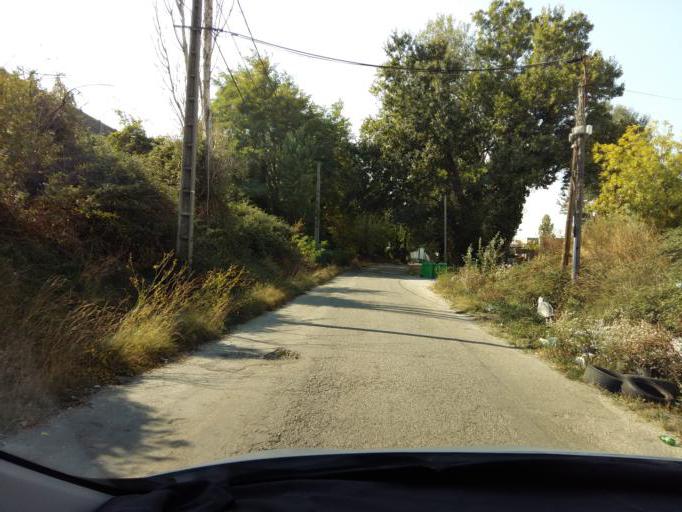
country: FR
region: Provence-Alpes-Cote d'Azur
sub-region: Departement du Vaucluse
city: Avignon
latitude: 43.9388
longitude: 4.7902
